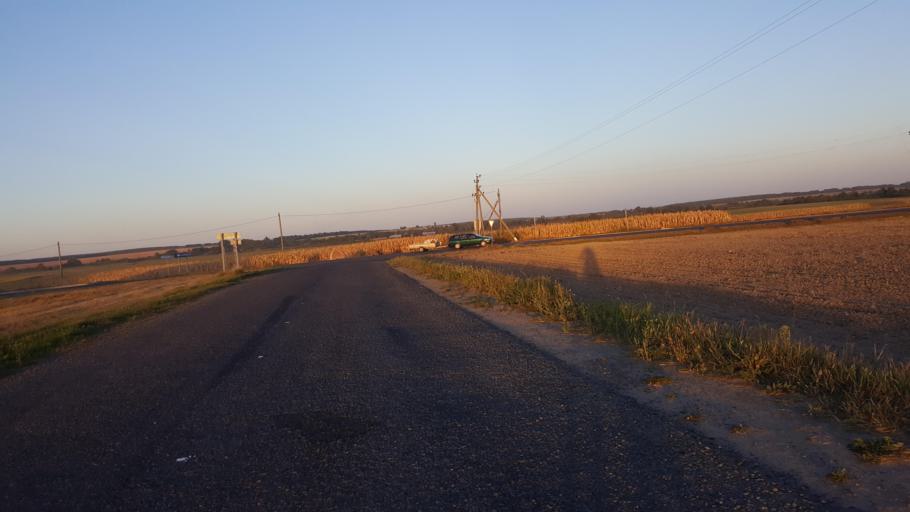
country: BY
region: Brest
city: Charnawchytsy
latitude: 52.2970
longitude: 23.6056
